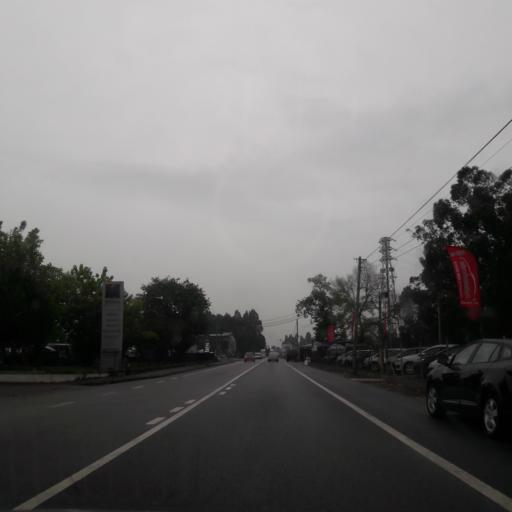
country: PT
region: Porto
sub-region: Vila do Conde
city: Arvore
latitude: 41.3080
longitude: -8.7044
